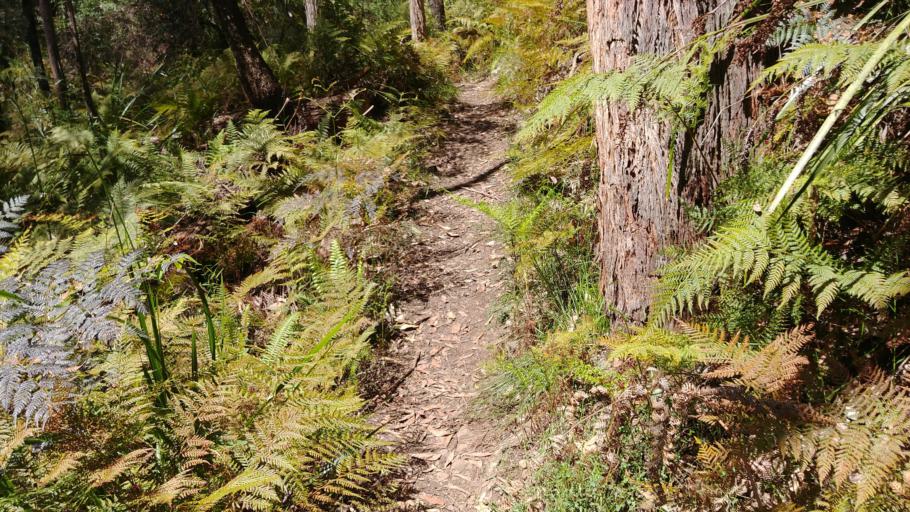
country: AU
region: Victoria
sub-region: Cardinia
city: Gembrook
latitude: -37.8965
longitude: 145.5703
